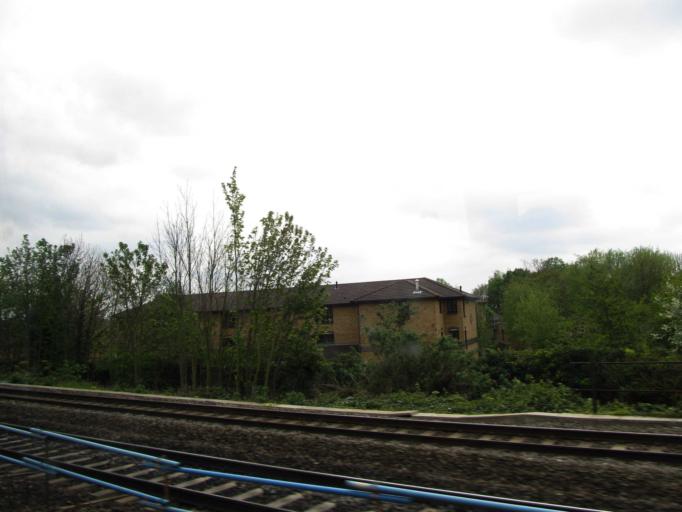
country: GB
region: England
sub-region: Greater London
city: West Drayton
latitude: 51.5100
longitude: -0.4774
